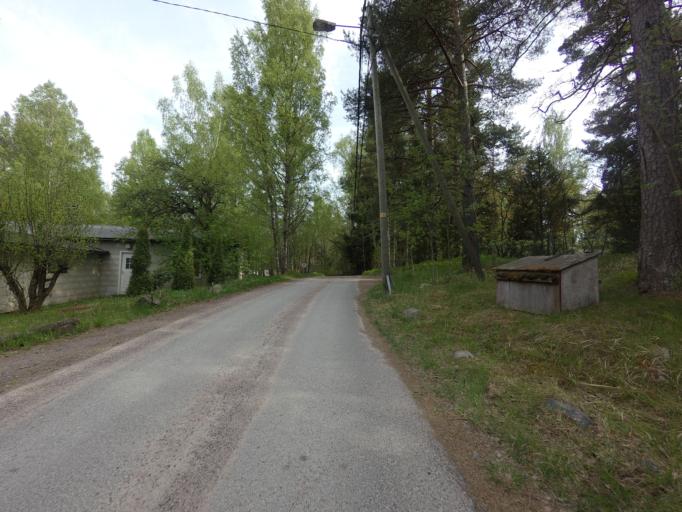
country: FI
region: Uusimaa
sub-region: Helsinki
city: Koukkuniemi
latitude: 60.1143
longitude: 24.6960
